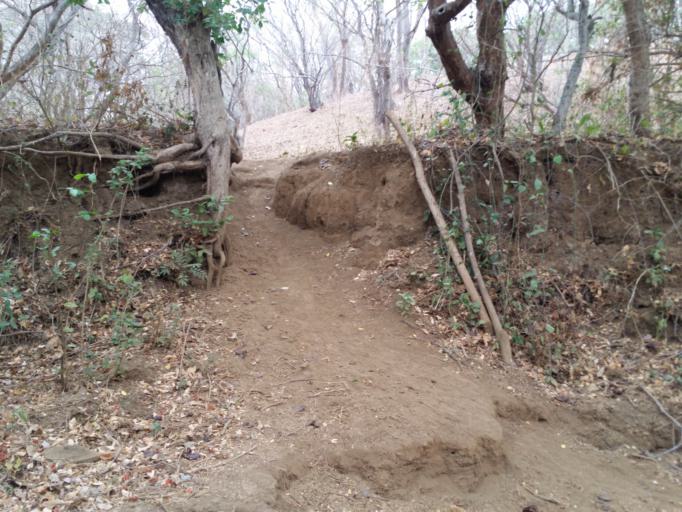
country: NI
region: Managua
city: Managua
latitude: 12.0861
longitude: -86.2507
